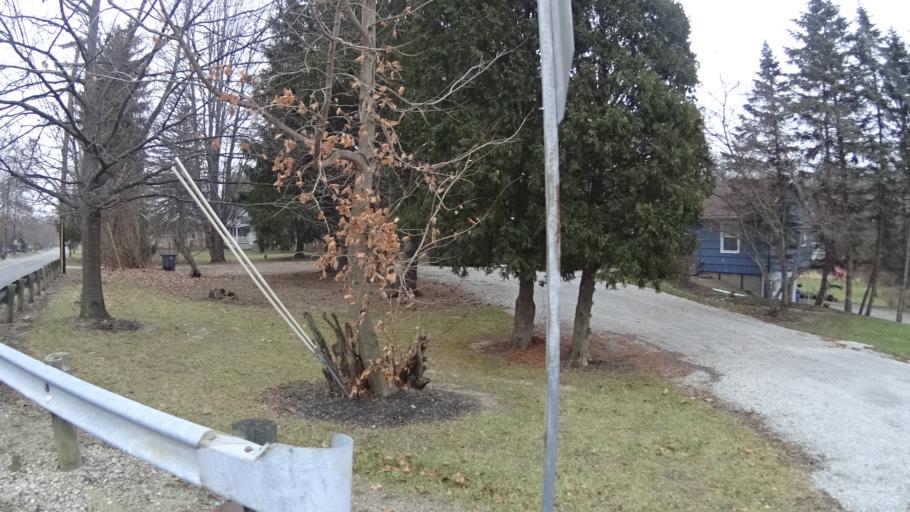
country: US
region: Ohio
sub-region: Lorain County
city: Oberlin
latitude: 41.2914
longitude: -82.1973
